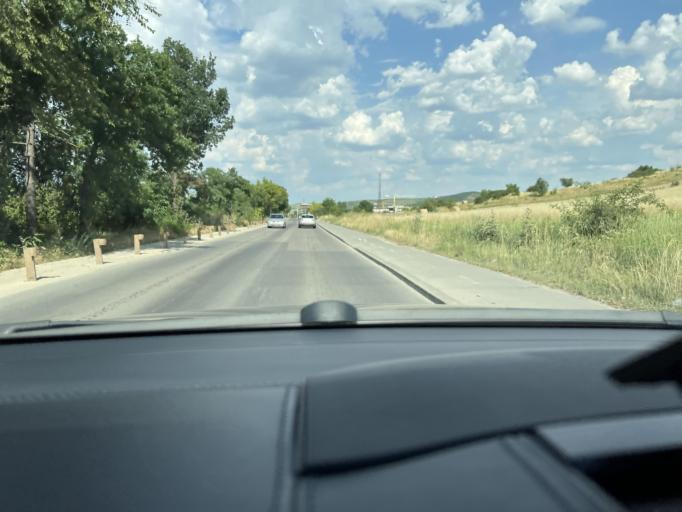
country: RO
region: Cluj
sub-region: Comuna Apahida
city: Dezmir
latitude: 46.7792
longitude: 23.6761
